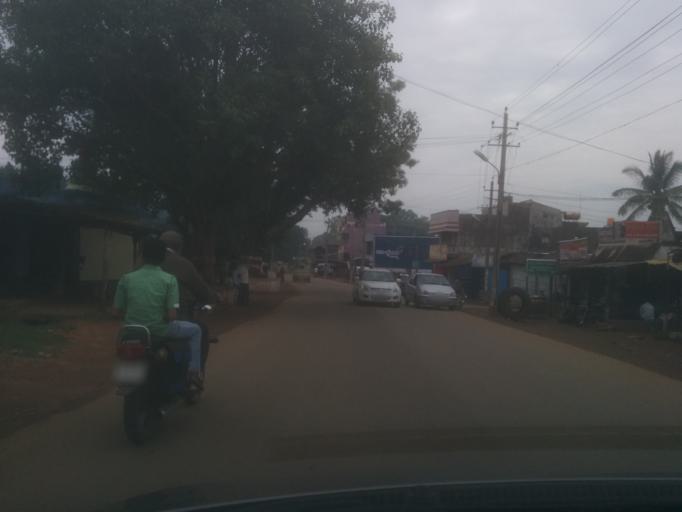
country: IN
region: Karnataka
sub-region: Chikmagalur
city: Chikmagalur
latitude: 13.3379
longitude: 75.7698
